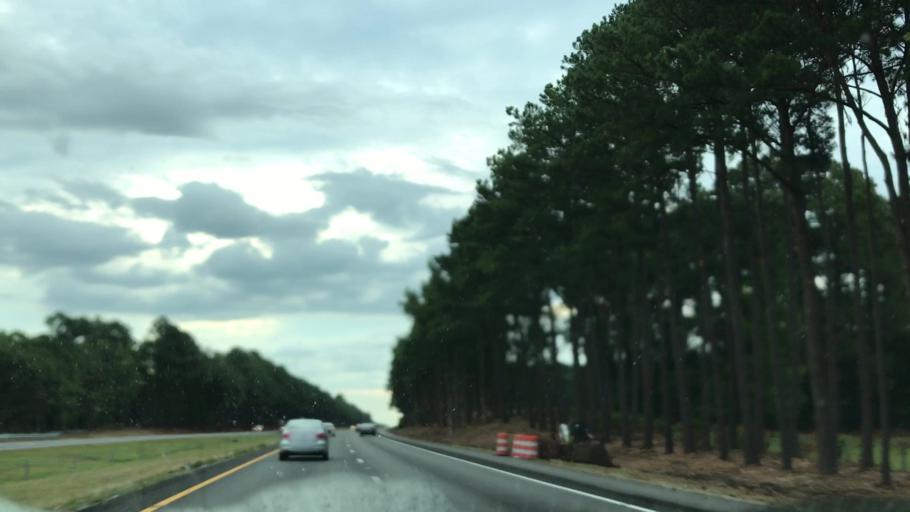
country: US
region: North Carolina
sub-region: Johnston County
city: Four Oaks
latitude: 35.4139
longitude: -78.4717
